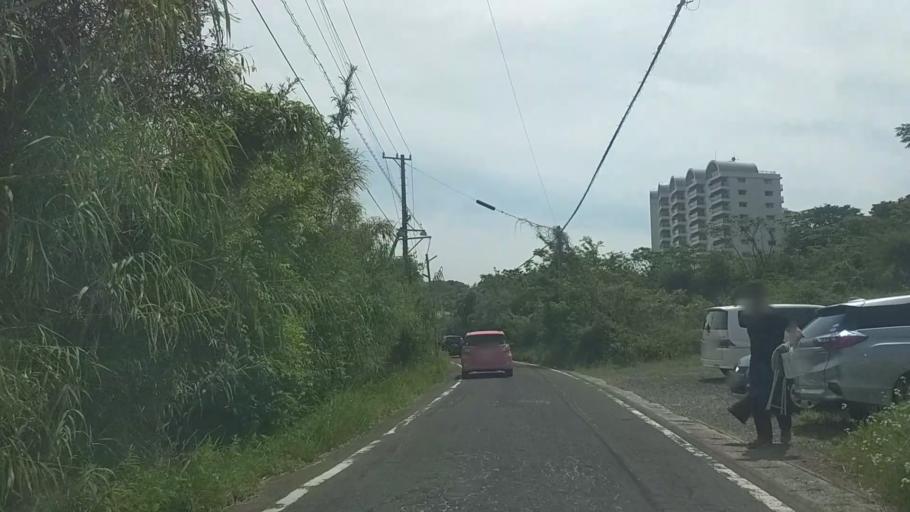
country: JP
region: Shizuoka
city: Kosai-shi
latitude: 34.7784
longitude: 137.5696
